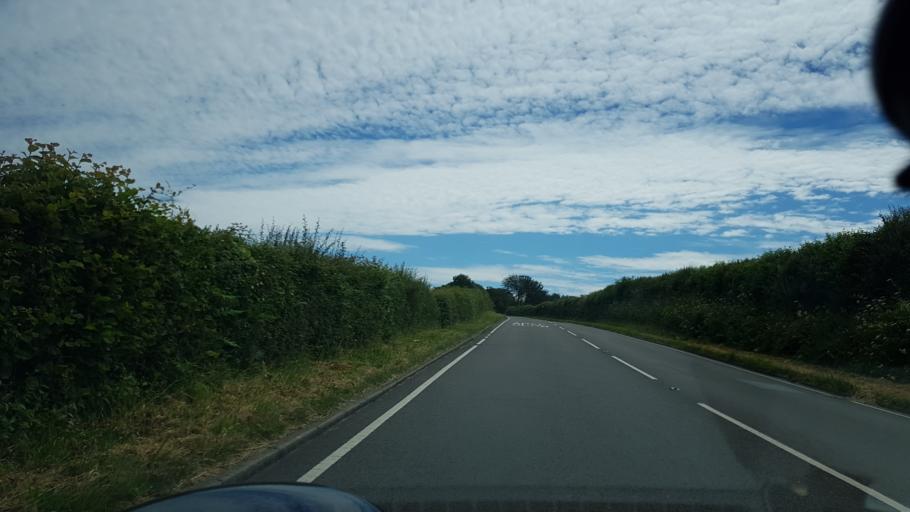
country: GB
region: Wales
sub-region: Carmarthenshire
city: Saint Clears
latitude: 51.7878
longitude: -4.4806
